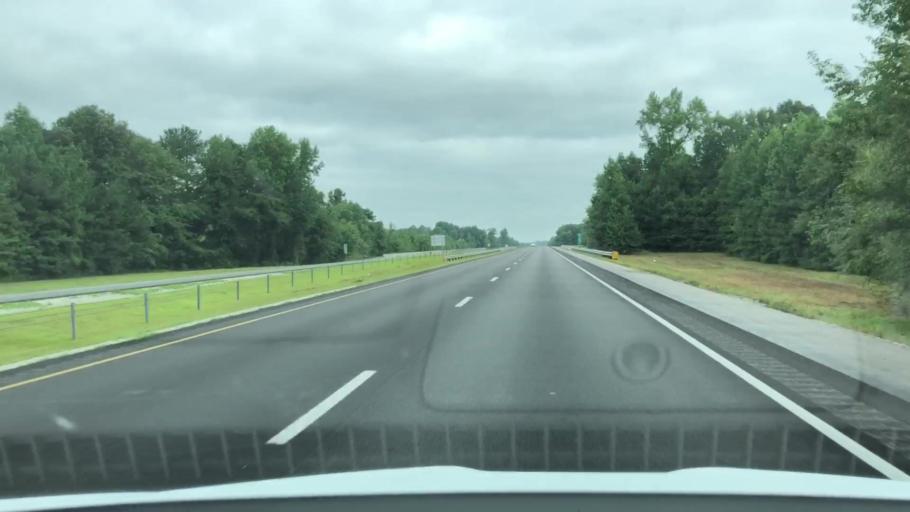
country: US
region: North Carolina
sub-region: Wayne County
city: Fremont
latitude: 35.5598
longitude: -77.9874
